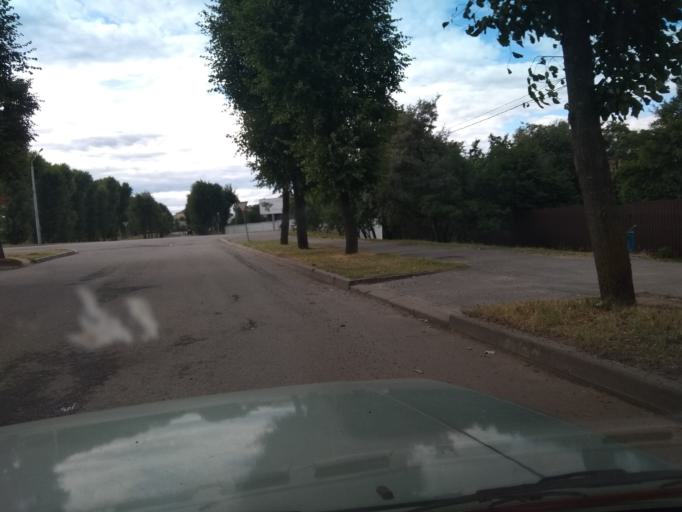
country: BY
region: Mogilev
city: Mahilyow
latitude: 53.9254
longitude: 30.3510
